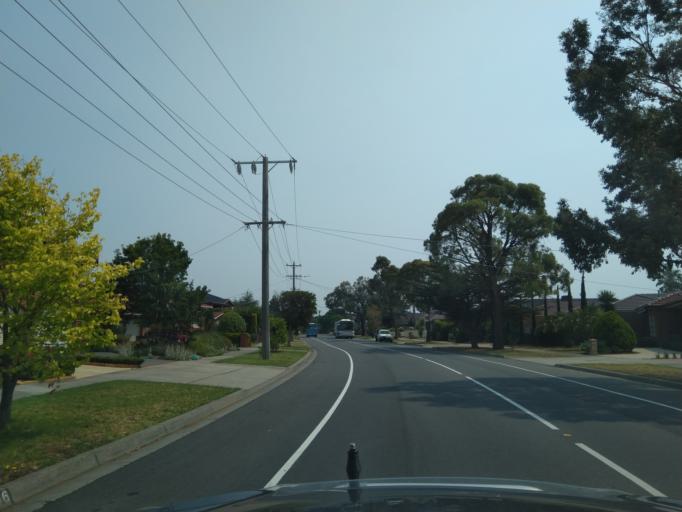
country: AU
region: Victoria
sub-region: Hume
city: Meadow Heights
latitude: -37.6458
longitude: 144.8982
